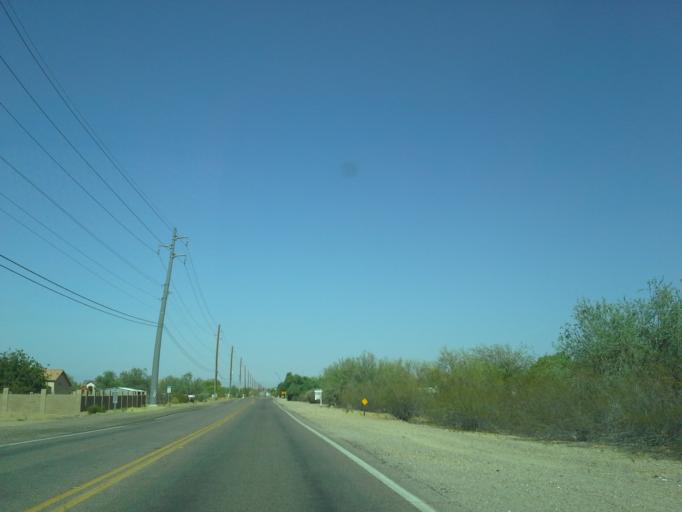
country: US
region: Arizona
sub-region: Maricopa County
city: Queen Creek
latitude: 33.2048
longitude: -111.6589
